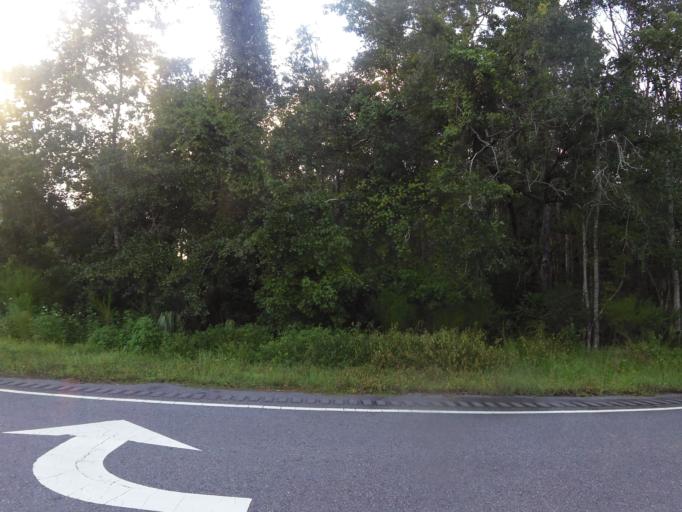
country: US
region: Georgia
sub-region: Camden County
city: St Marys
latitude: 30.7609
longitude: -81.6031
